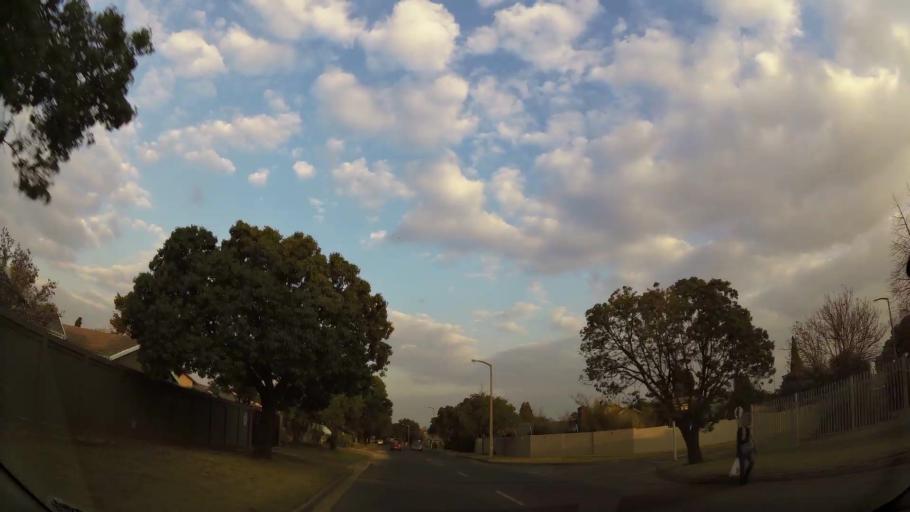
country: ZA
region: Gauteng
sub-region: Ekurhuleni Metropolitan Municipality
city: Benoni
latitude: -26.1687
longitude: 28.3002
